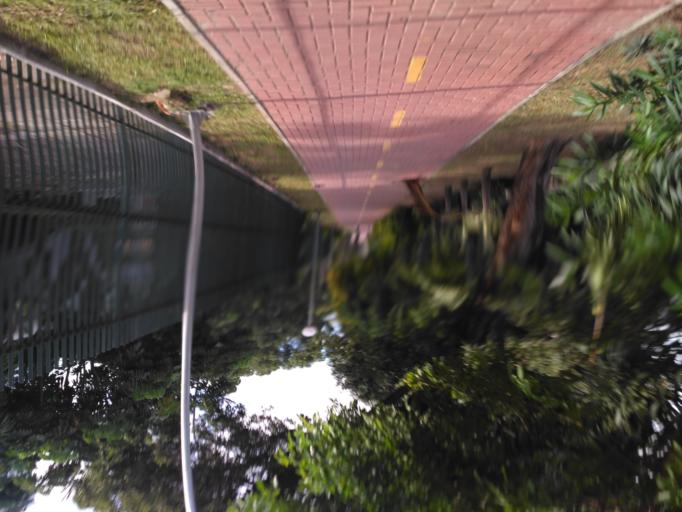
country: BR
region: Pernambuco
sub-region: Recife
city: Recife
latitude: -8.0515
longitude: -34.8744
